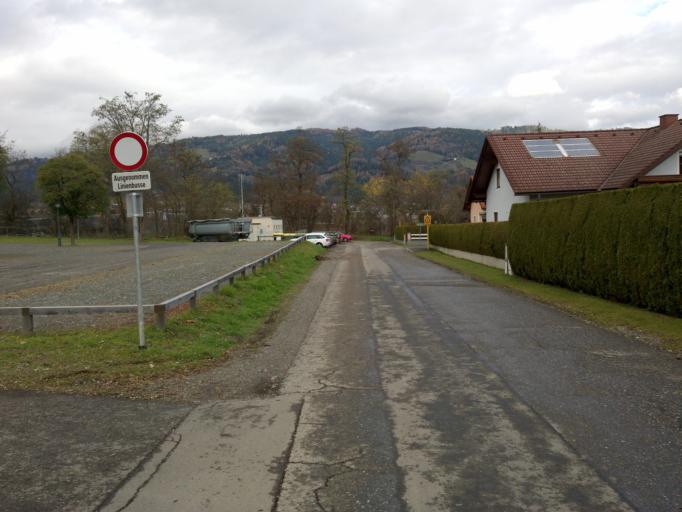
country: AT
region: Styria
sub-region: Politischer Bezirk Murtal
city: Fohnsdorf
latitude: 47.1914
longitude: 14.6751
